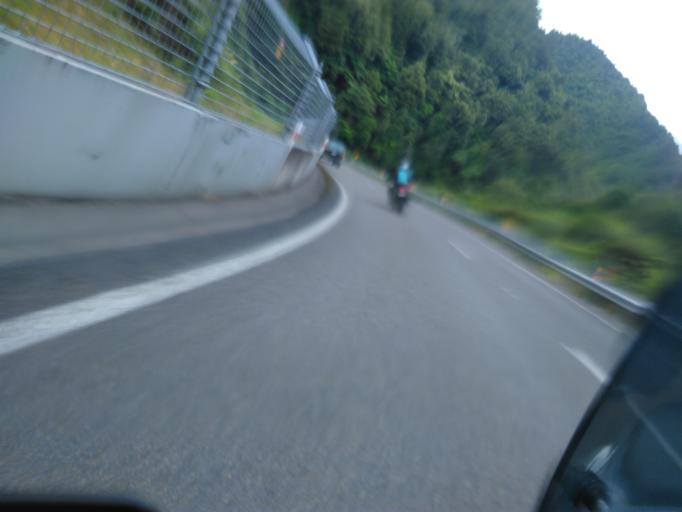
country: NZ
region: Bay of Plenty
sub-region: Opotiki District
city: Opotiki
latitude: -38.3113
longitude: 177.3948
